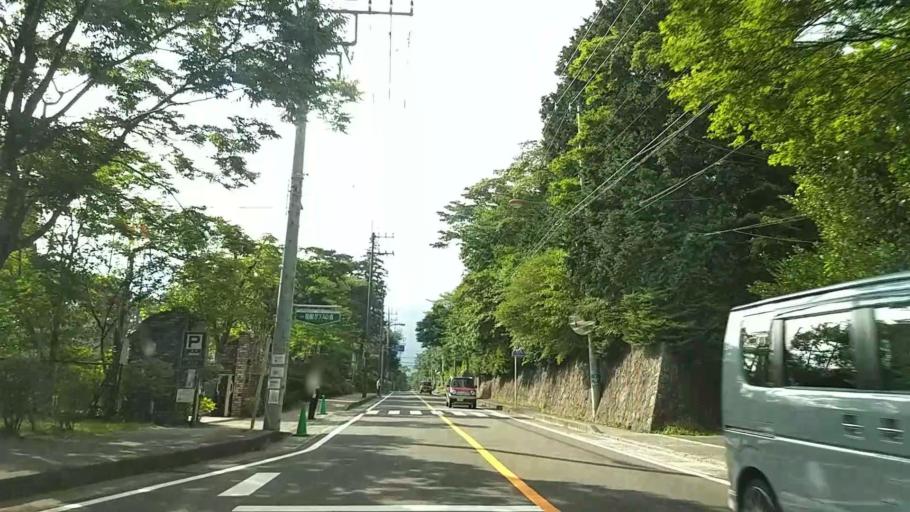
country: JP
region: Kanagawa
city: Hakone
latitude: 35.2664
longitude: 139.0184
